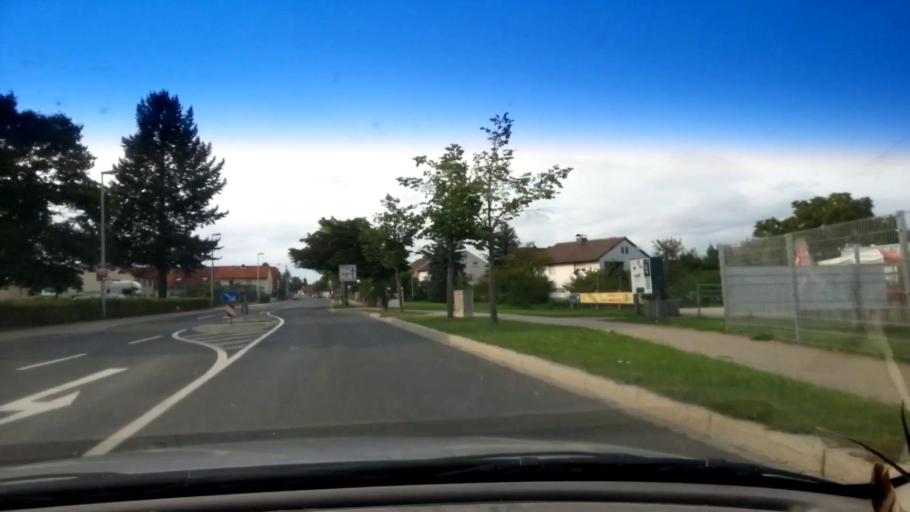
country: DE
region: Bavaria
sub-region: Upper Franconia
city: Strullendorf
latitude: 49.8411
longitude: 10.9727
